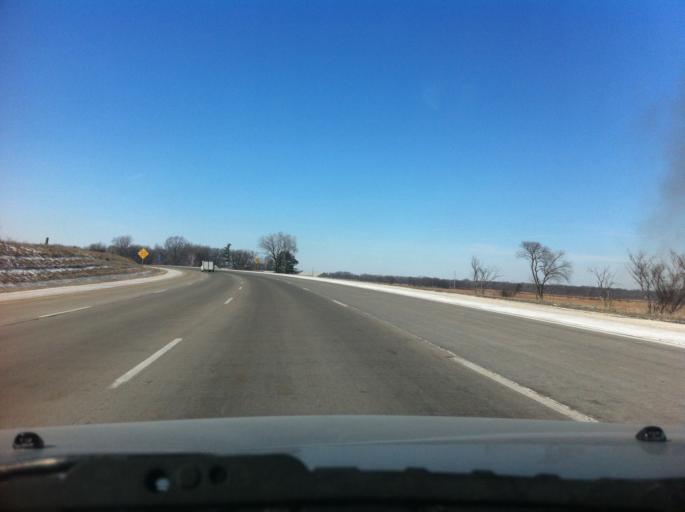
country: US
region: Wisconsin
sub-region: Columbia County
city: Portage
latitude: 43.4669
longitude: -89.4955
